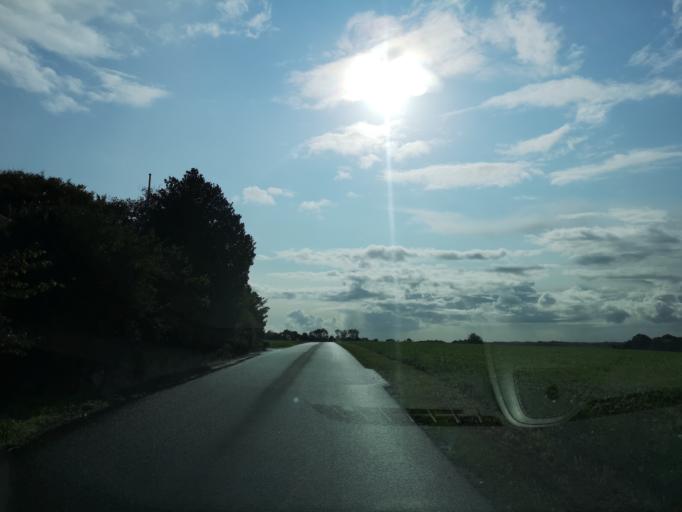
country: DK
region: Central Jutland
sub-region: Ringkobing-Skjern Kommune
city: Skjern
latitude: 55.9853
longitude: 8.5508
